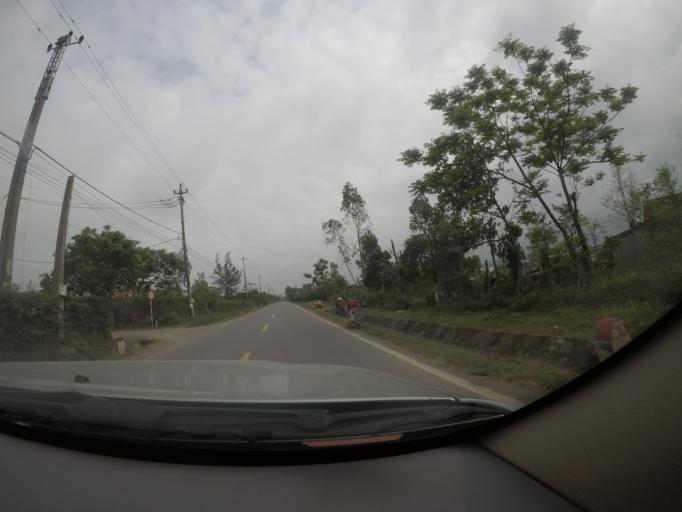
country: VN
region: Quang Binh
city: Kwang Binh
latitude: 17.4341
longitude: 106.5817
